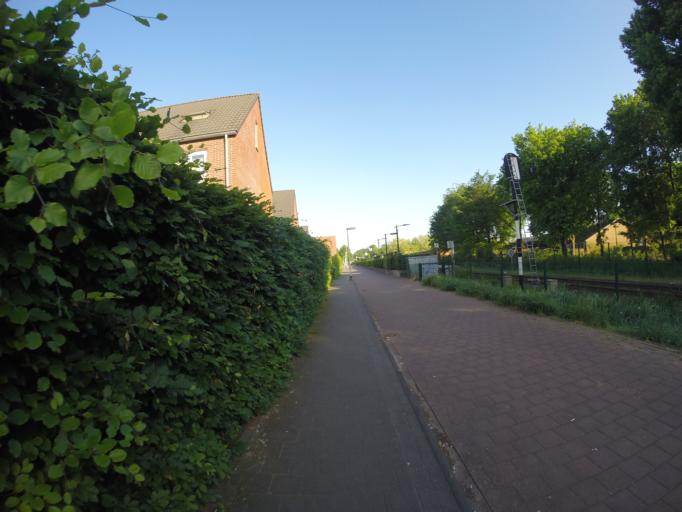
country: NL
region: Gelderland
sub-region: Oude IJsselstreek
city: Gendringen
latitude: 51.9299
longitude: 6.3505
